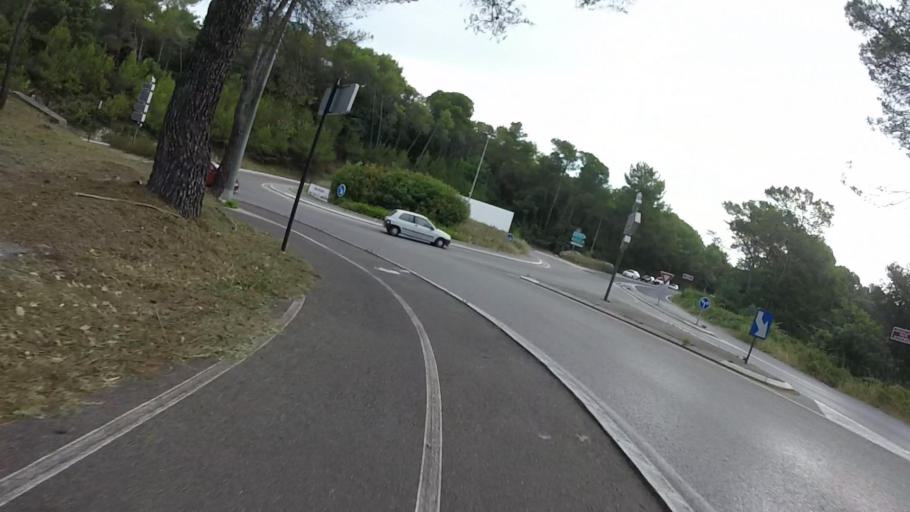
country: FR
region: Provence-Alpes-Cote d'Azur
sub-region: Departement des Alpes-Maritimes
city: Le Cannet
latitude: 43.6016
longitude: 7.0356
